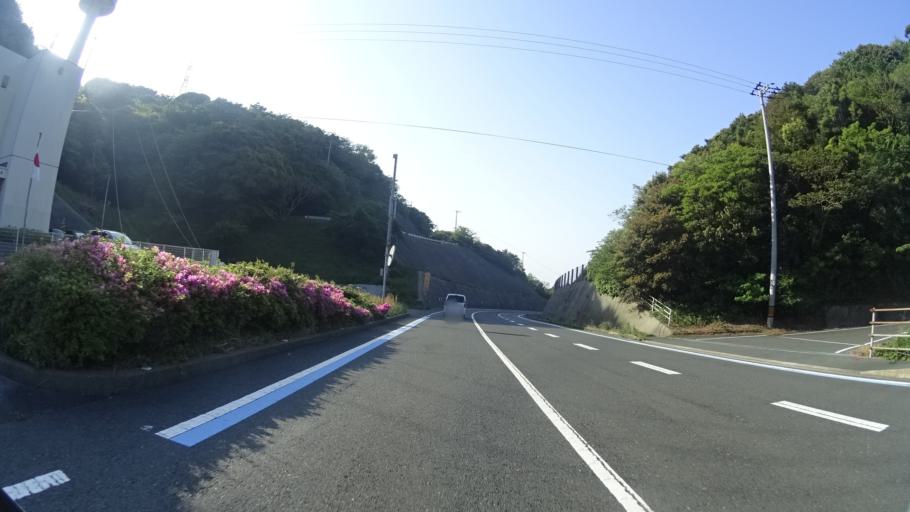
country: JP
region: Ehime
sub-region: Nishiuwa-gun
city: Ikata-cho
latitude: 33.4109
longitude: 132.1725
